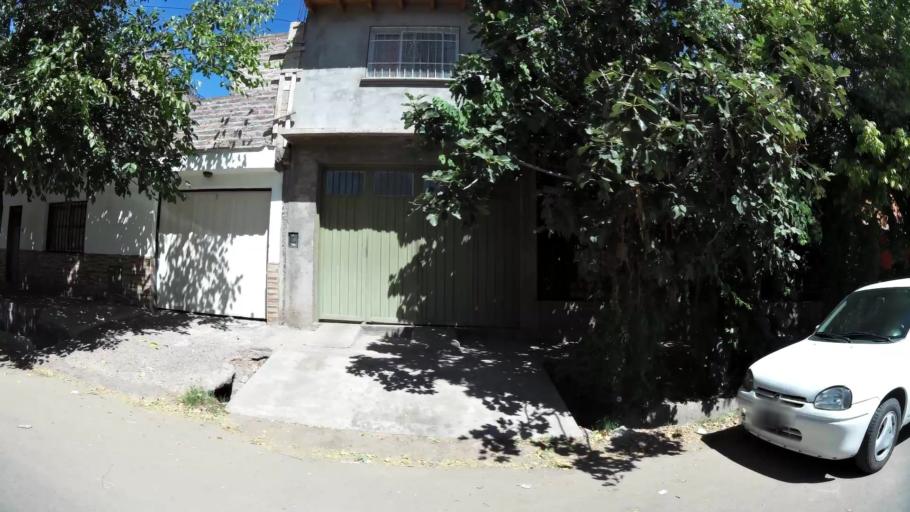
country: AR
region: Mendoza
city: Villa Nueva
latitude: -32.8808
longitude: -68.7875
